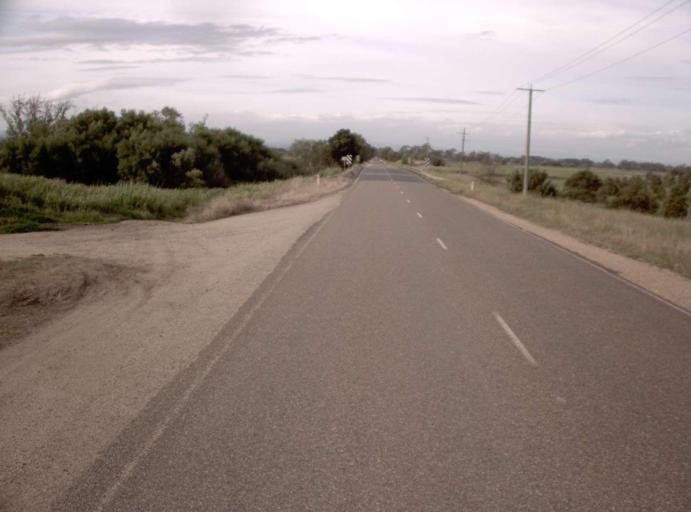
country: AU
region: Victoria
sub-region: Wellington
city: Heyfield
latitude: -37.9839
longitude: 146.8876
